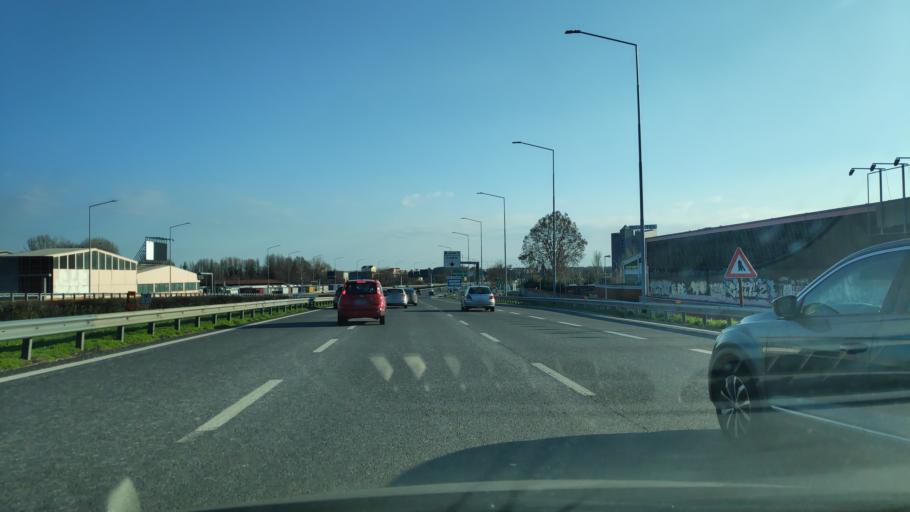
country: IT
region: Lombardy
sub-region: Citta metropolitana di Milano
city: Linate
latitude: 45.4518
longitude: 9.2566
